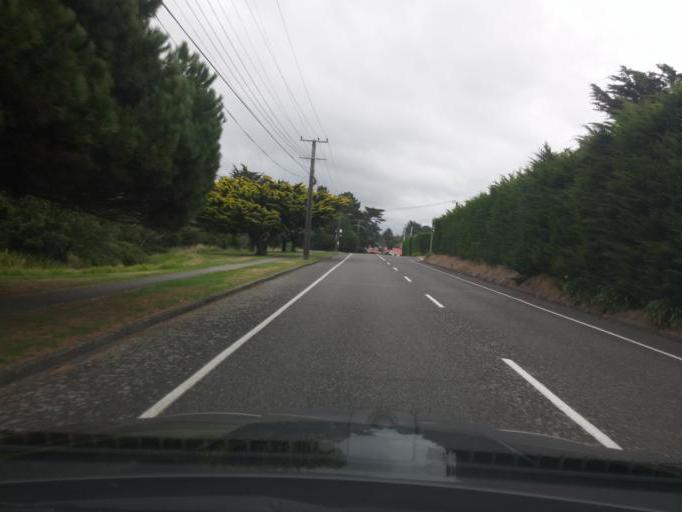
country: NZ
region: Wellington
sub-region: Kapiti Coast District
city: Paraparaumu
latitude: -40.8621
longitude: 175.0290
